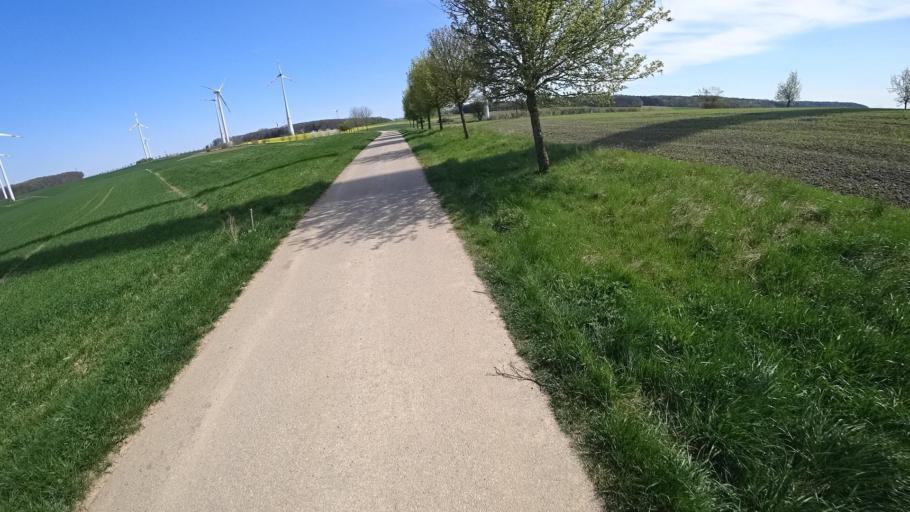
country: DE
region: Rheinland-Pfalz
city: Eisenach
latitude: 49.8452
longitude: 6.5200
